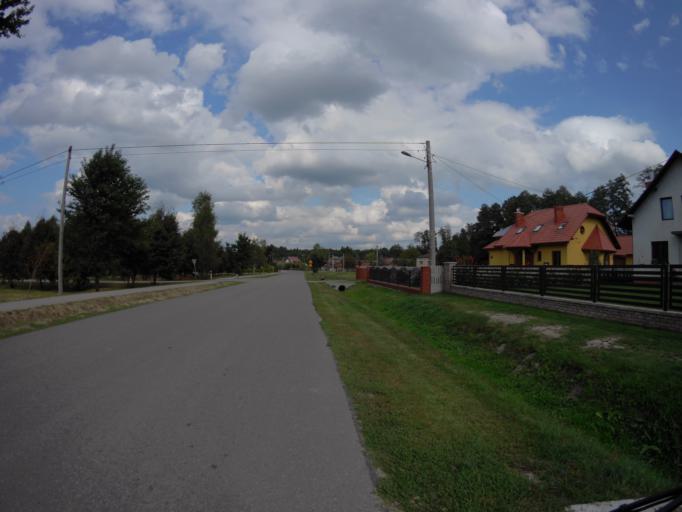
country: PL
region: Subcarpathian Voivodeship
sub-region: Powiat lezajski
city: Brzoza Krolewska
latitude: 50.2703
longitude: 22.3501
